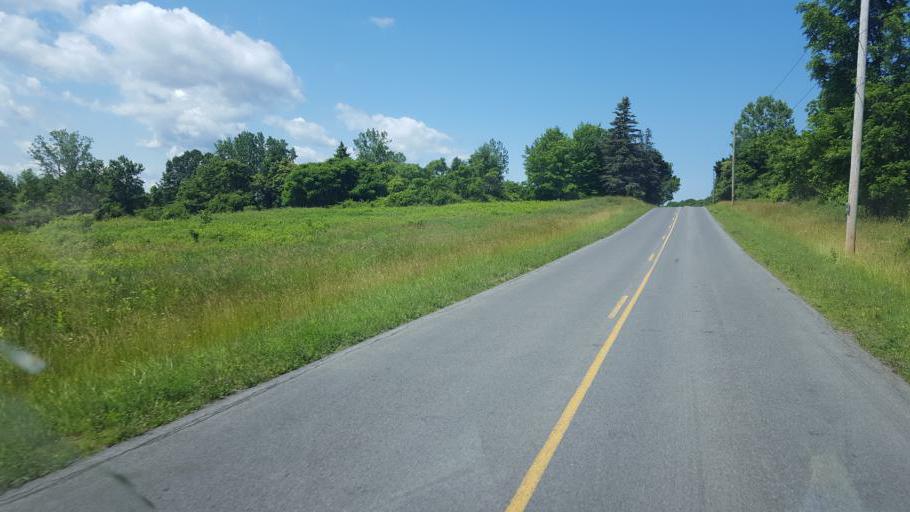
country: US
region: New York
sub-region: Wayne County
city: Wolcott
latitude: 43.2802
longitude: -76.9175
